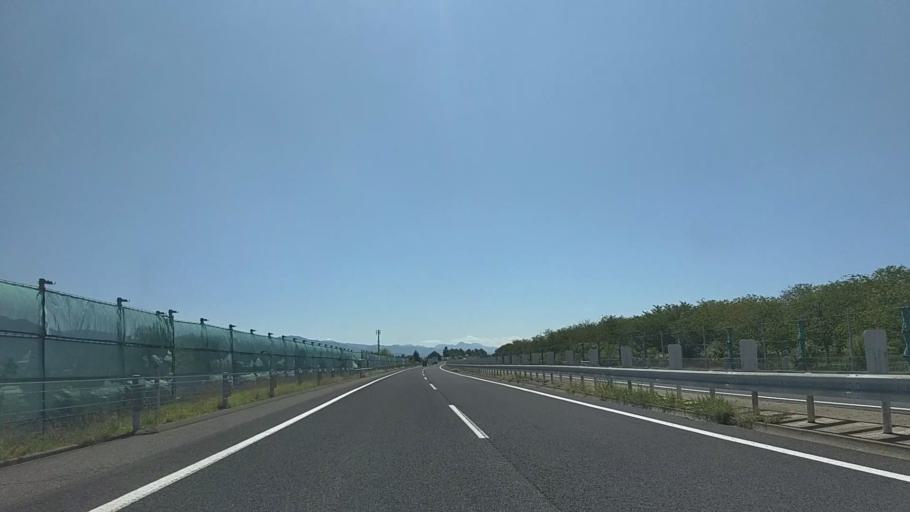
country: JP
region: Nagano
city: Suzaka
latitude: 36.7100
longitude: 138.3085
